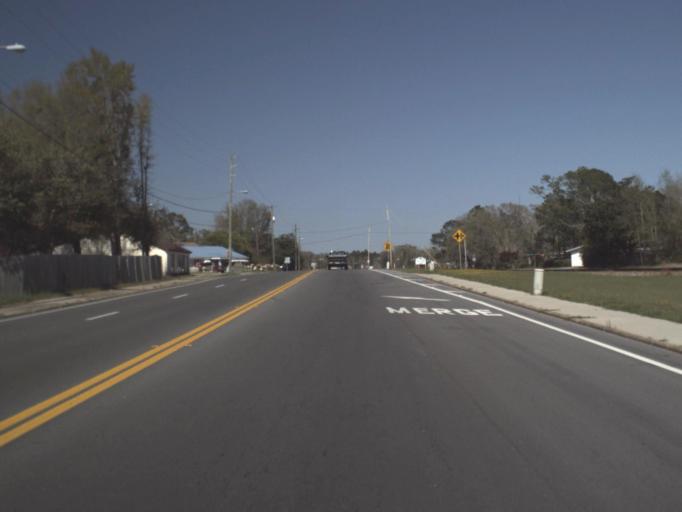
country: US
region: Florida
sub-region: Walton County
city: DeFuniak Springs
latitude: 30.7214
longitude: -86.1011
